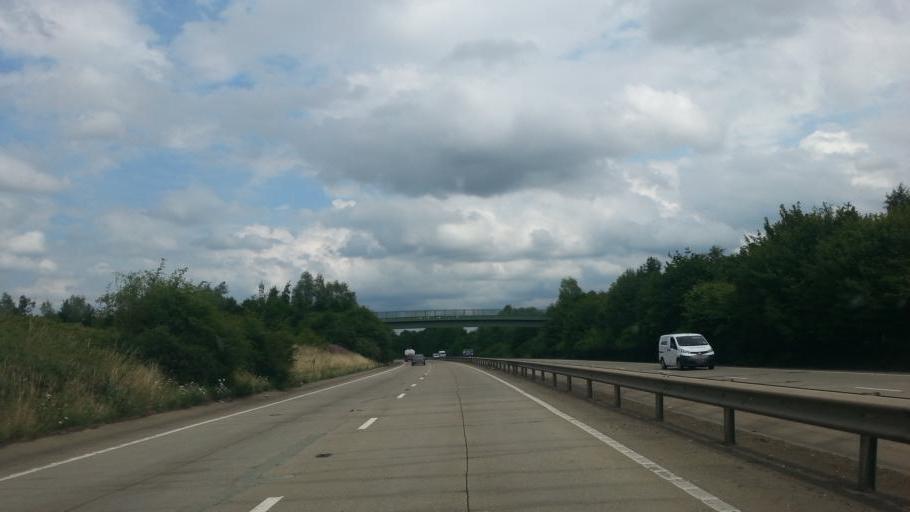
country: GB
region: England
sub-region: Norfolk
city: Hethersett
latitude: 52.5598
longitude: 1.1307
